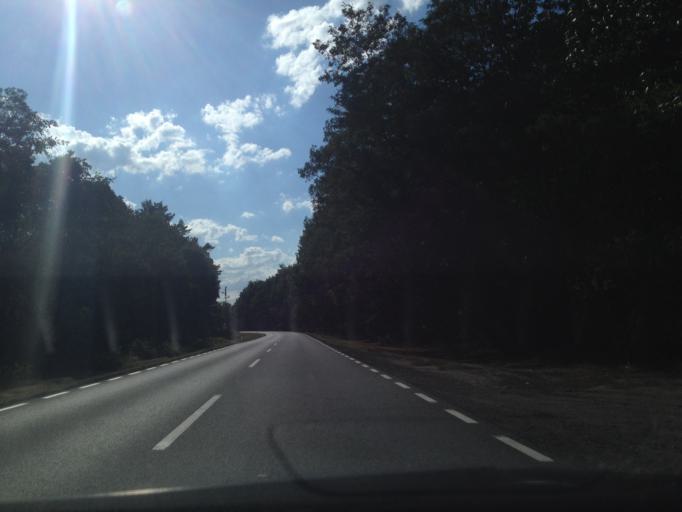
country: PL
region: Lubusz
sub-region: Powiat zarski
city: Tuplice
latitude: 51.6375
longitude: 14.9059
